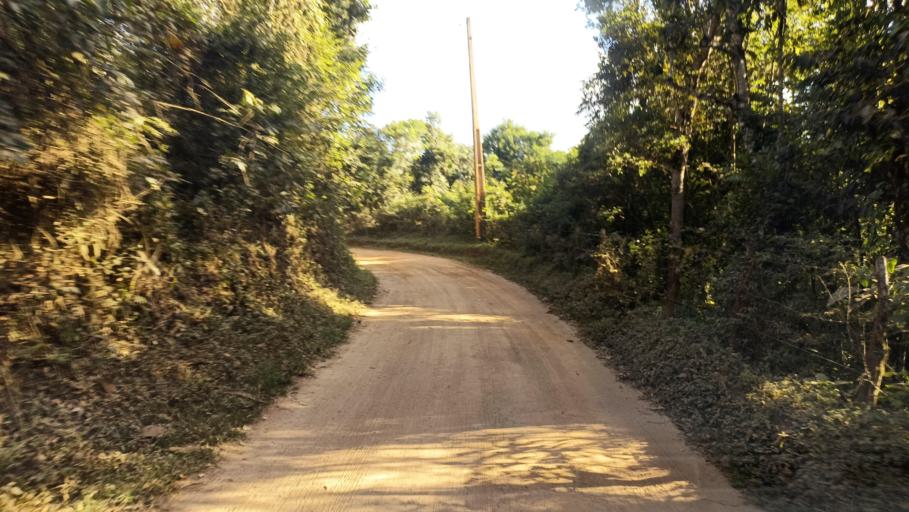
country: BR
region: Minas Gerais
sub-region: Ouro Preto
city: Ouro Preto
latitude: -20.3062
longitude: -43.5770
